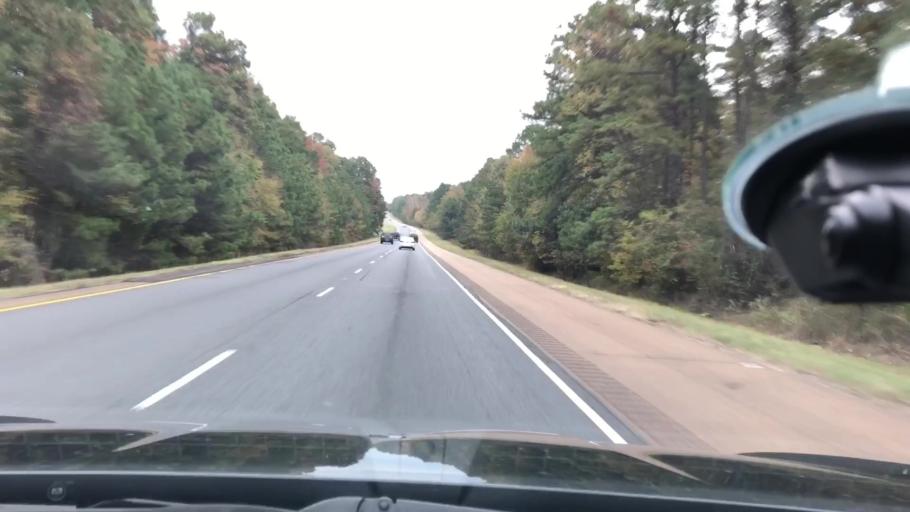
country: US
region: Arkansas
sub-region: Clark County
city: Gurdon
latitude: 33.9417
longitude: -93.2441
